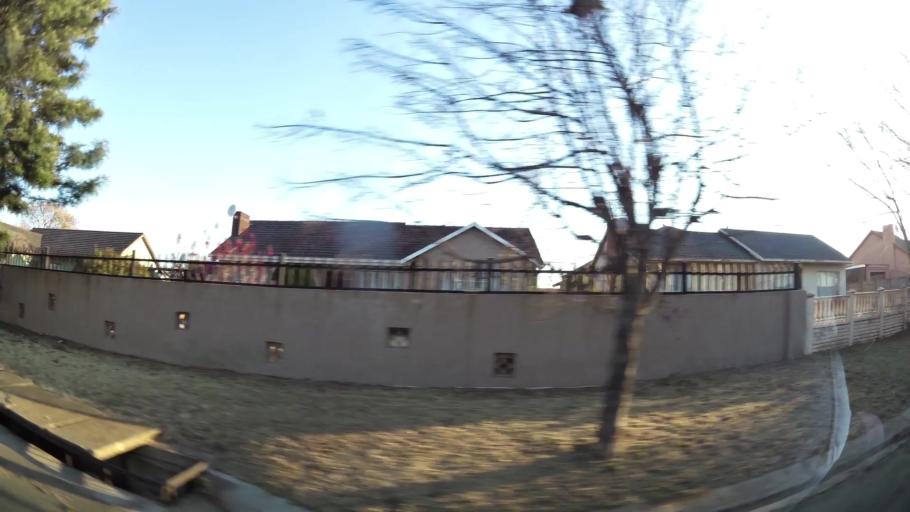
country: ZA
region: Gauteng
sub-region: West Rand District Municipality
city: Randfontein
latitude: -26.2054
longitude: 27.6565
